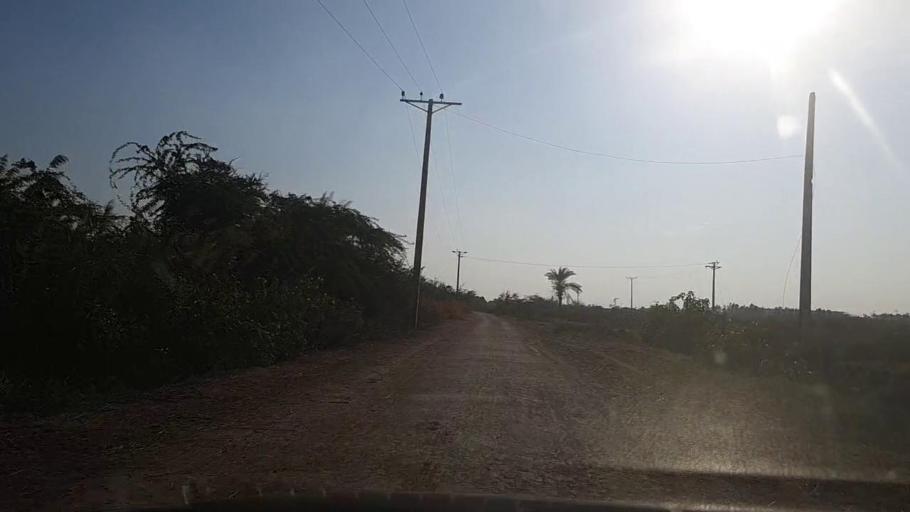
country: PK
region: Sindh
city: Gharo
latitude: 24.7112
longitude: 67.6841
